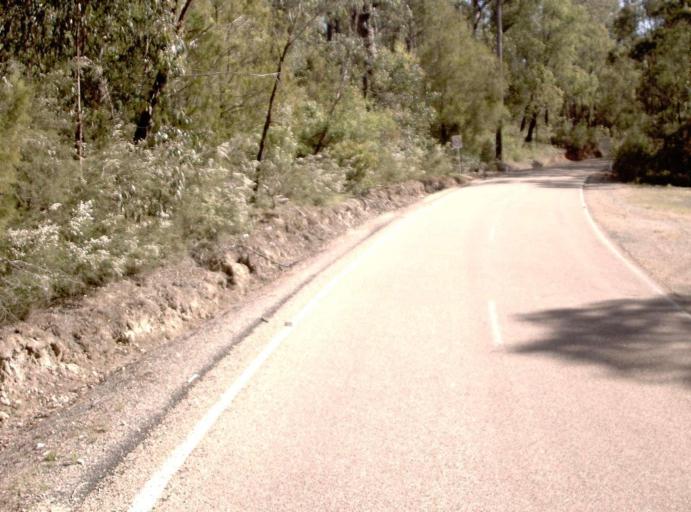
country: AU
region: Victoria
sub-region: East Gippsland
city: Lakes Entrance
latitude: -37.5003
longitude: 148.5506
